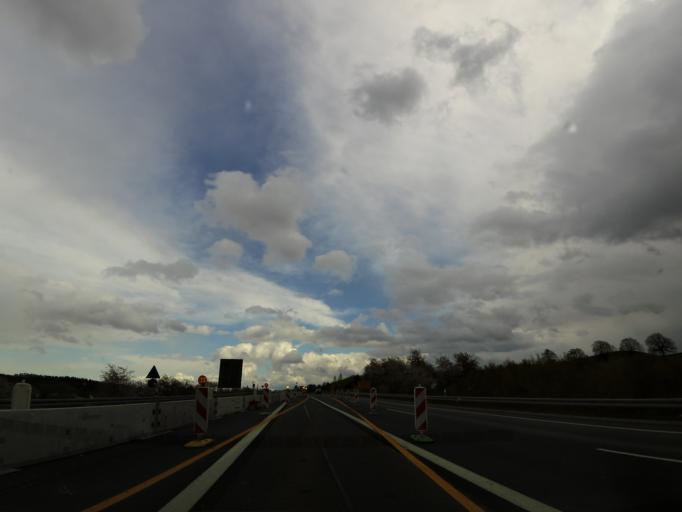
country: DE
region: Saxony-Anhalt
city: Blankenburg
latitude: 51.8200
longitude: 10.9294
